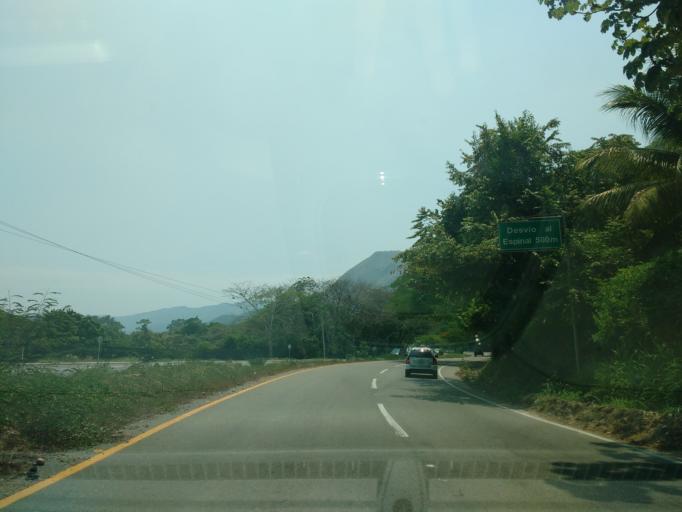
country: CO
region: Cundinamarca
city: Ricaurte
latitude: 4.2462
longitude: -74.7385
